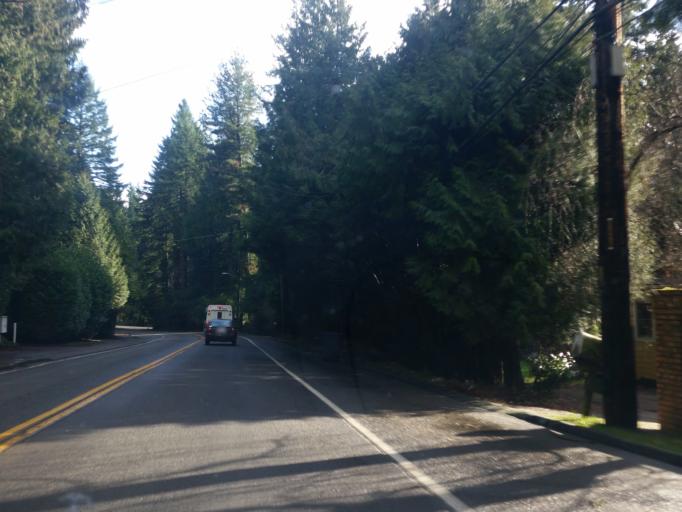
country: US
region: Washington
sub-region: King County
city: Lake Forest Park
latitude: 47.7614
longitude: -122.2875
